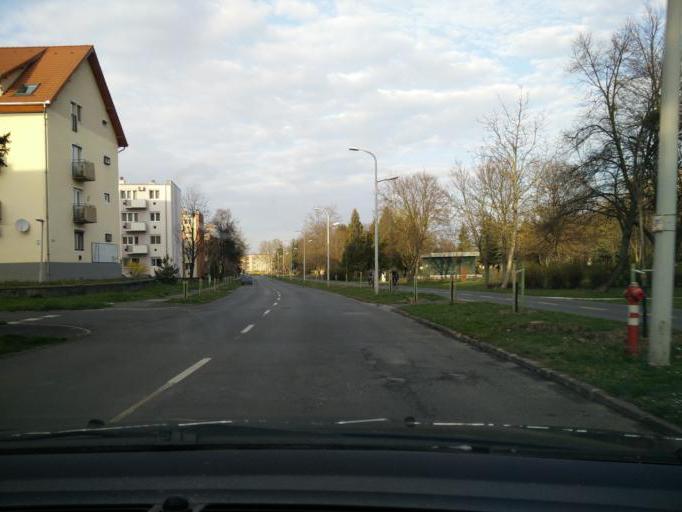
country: HU
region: Zala
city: Zalaegerszeg
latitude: 46.8400
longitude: 16.8364
